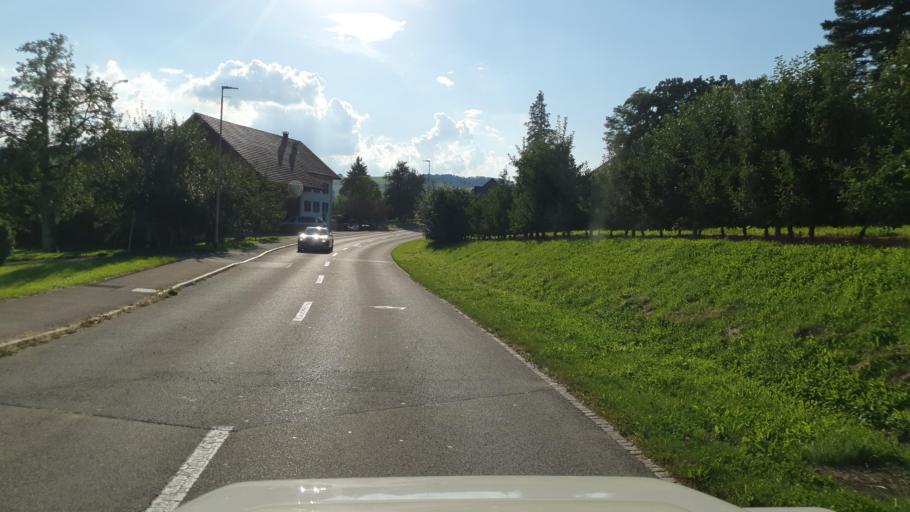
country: CH
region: Aargau
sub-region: Bezirk Muri
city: Waltenschwil
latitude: 47.3108
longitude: 8.3266
